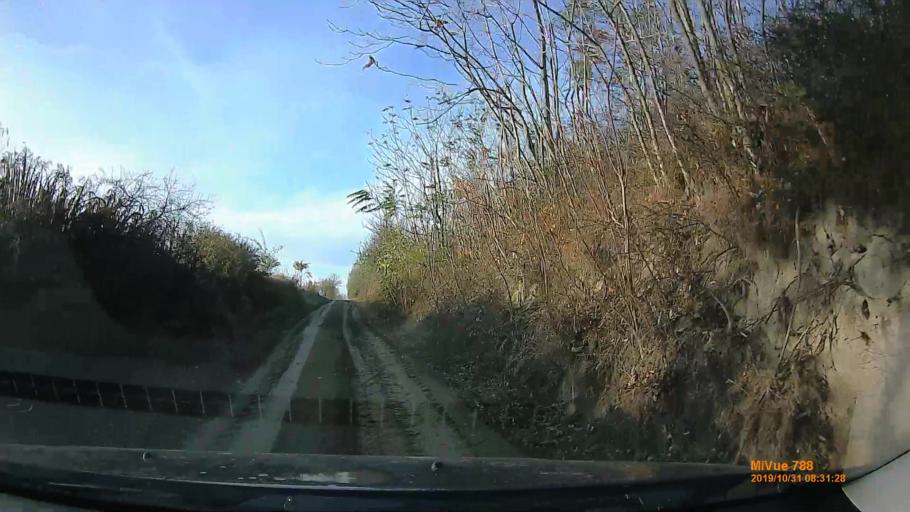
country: HU
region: Pest
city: Tapiobicske
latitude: 47.3473
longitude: 19.6658
